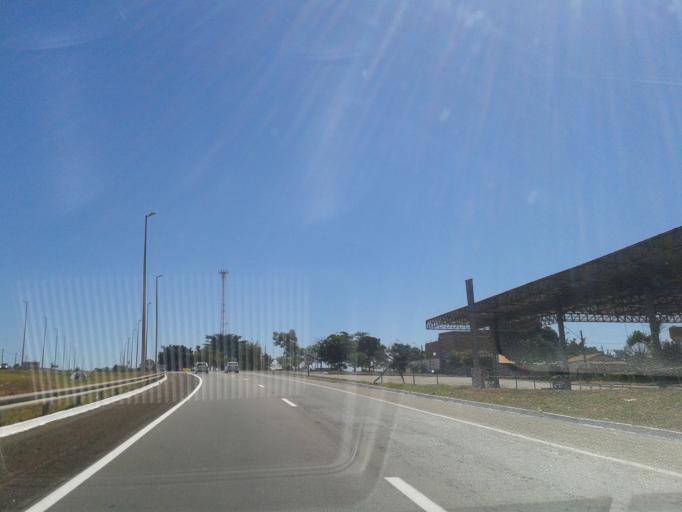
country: BR
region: Goias
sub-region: Goianira
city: Goianira
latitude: -16.5924
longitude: -49.3767
